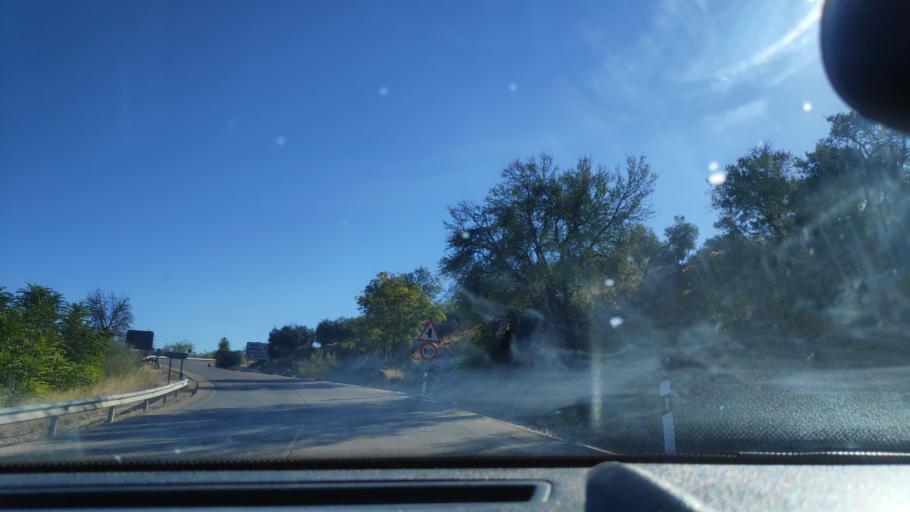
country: ES
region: Andalusia
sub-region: Provincia de Jaen
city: Jimena
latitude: 37.8450
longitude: -3.4900
